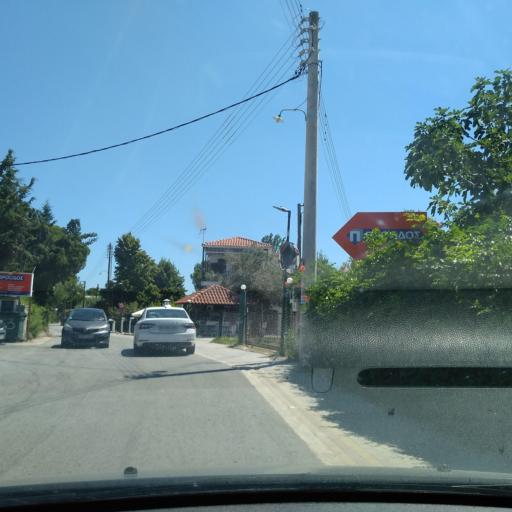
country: GR
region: Central Macedonia
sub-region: Nomos Chalkidikis
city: Neos Marmaras
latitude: 40.1870
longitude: 23.7932
